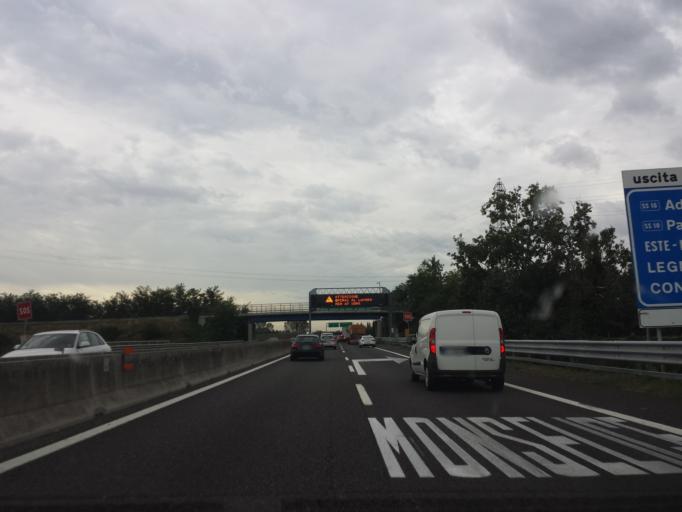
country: IT
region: Veneto
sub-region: Provincia di Padova
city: Pernumia
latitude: 45.2454
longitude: 11.7745
